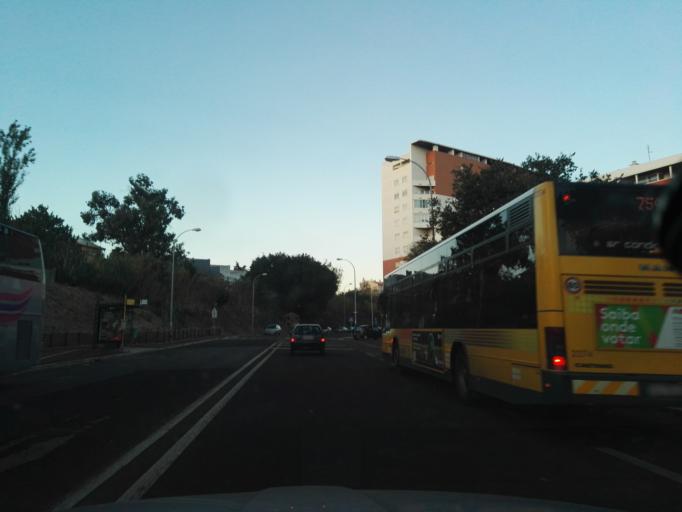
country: PT
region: Lisbon
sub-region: Amadora
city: Amadora
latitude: 38.7345
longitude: -9.2156
